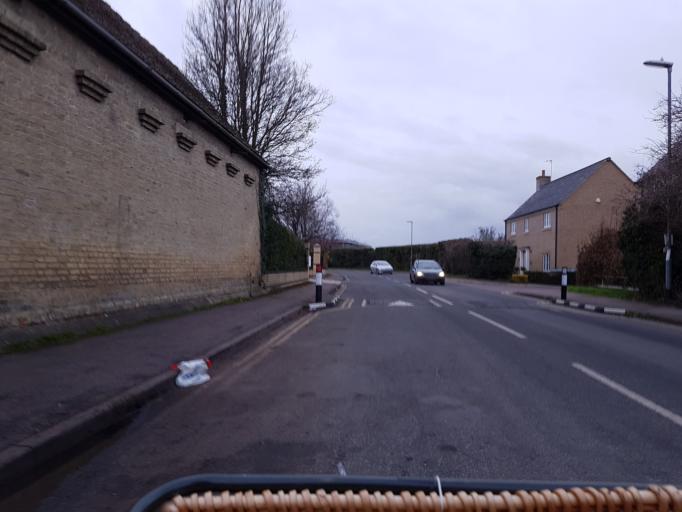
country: GB
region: England
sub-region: Cambridgeshire
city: Fulbourn
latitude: 52.1965
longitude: 0.1735
